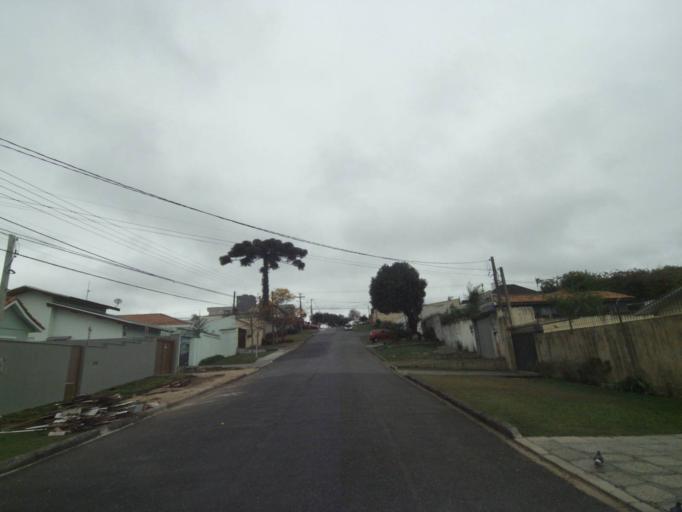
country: BR
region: Parana
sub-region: Curitiba
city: Curitiba
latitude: -25.4657
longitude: -49.2743
